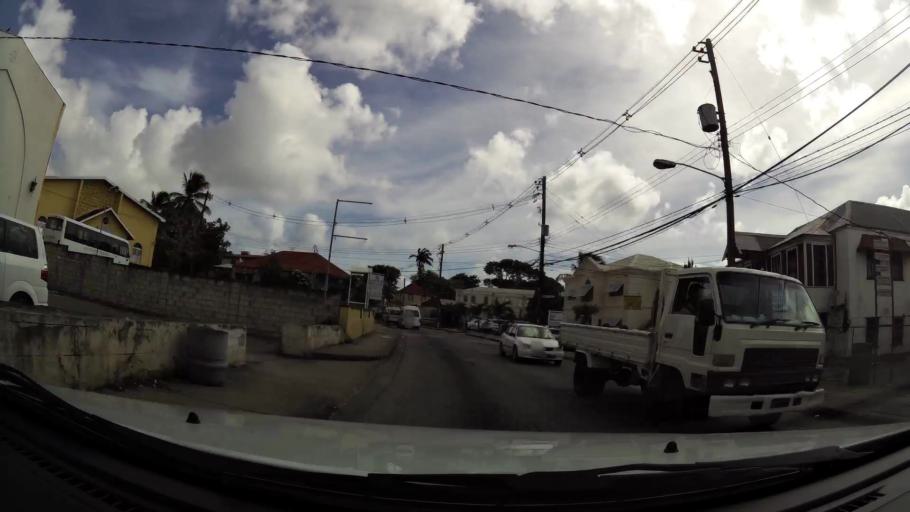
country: BB
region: Saint Michael
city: Bridgetown
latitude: 13.0948
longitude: -59.6084
